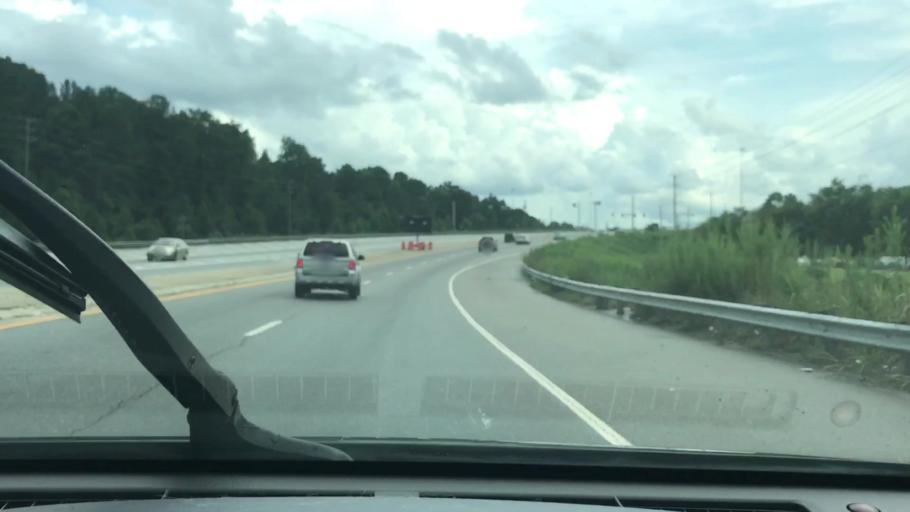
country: US
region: Georgia
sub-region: Newton County
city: Covington
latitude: 33.6168
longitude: -83.8238
